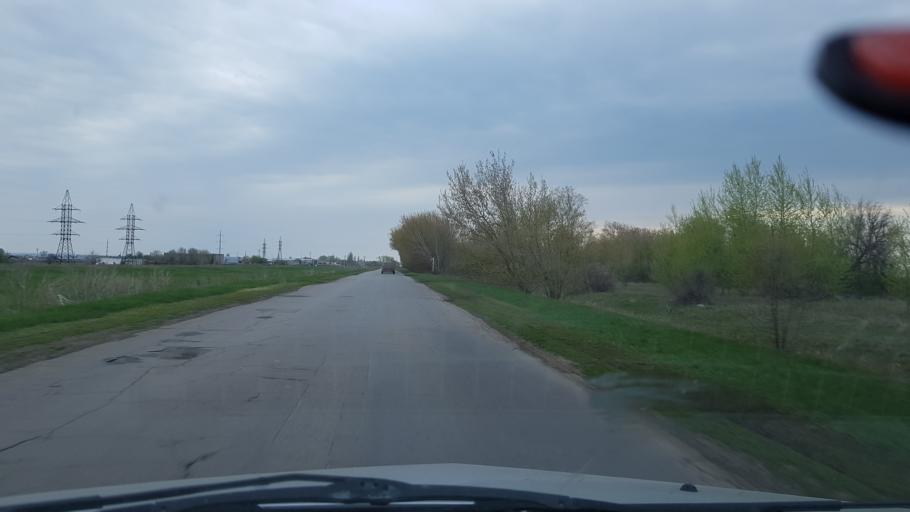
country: RU
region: Samara
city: Khryashchevka
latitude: 53.6717
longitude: 49.0951
